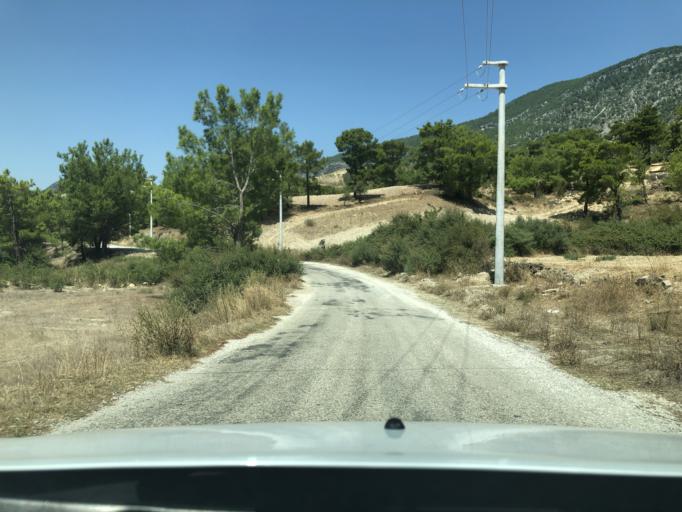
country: TR
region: Antalya
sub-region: Manavgat
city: Kizilagac
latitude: 36.8653
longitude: 31.5590
